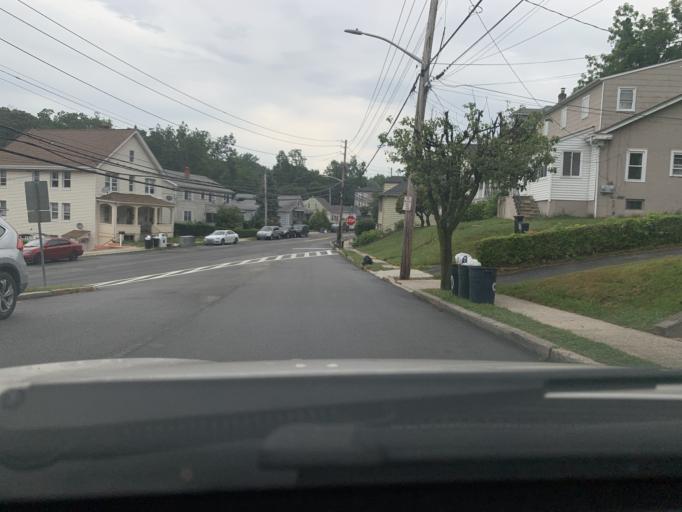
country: US
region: New York
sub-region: Westchester County
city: Ossining
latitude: 41.1684
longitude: -73.8551
